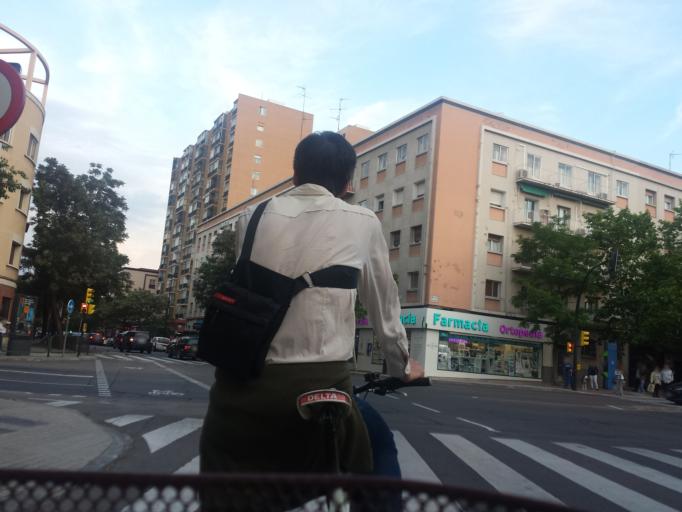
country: ES
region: Aragon
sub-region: Provincia de Zaragoza
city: Delicias
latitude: 41.6453
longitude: -0.9001
